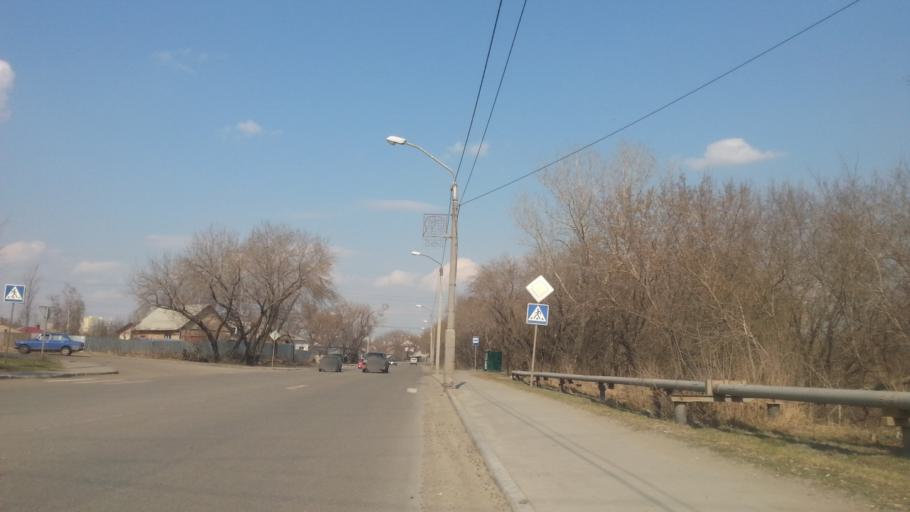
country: RU
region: Altai Krai
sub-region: Gorod Barnaulskiy
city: Barnaul
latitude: 53.3200
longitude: 83.7627
